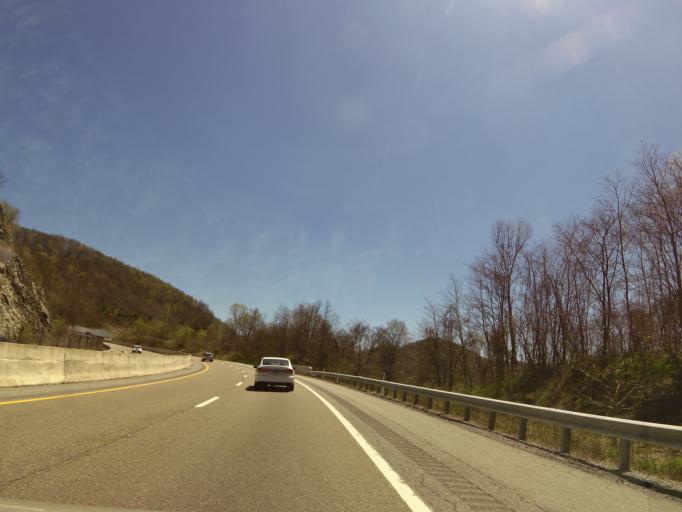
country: US
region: North Carolina
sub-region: Madison County
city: Mars Hill
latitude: 35.9656
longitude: -82.5555
